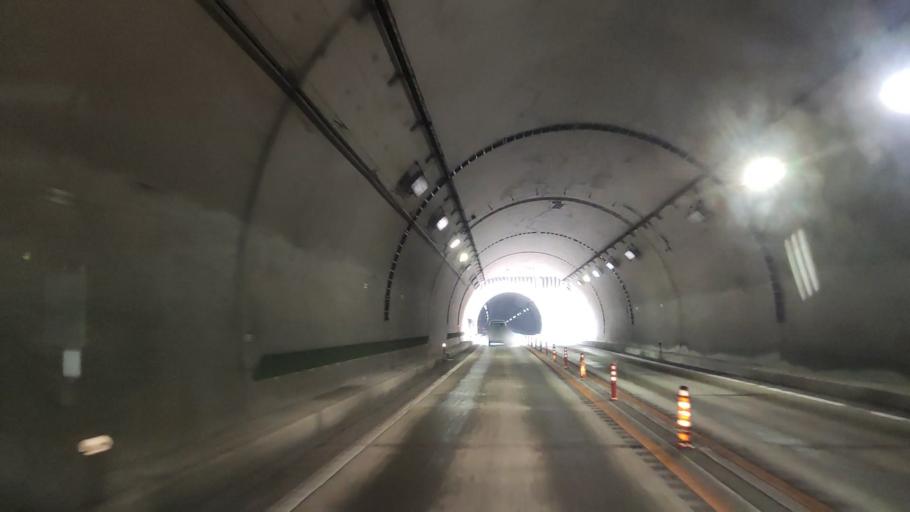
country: JP
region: Tokushima
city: Kamojimacho-jogejima
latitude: 34.1144
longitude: 134.3228
